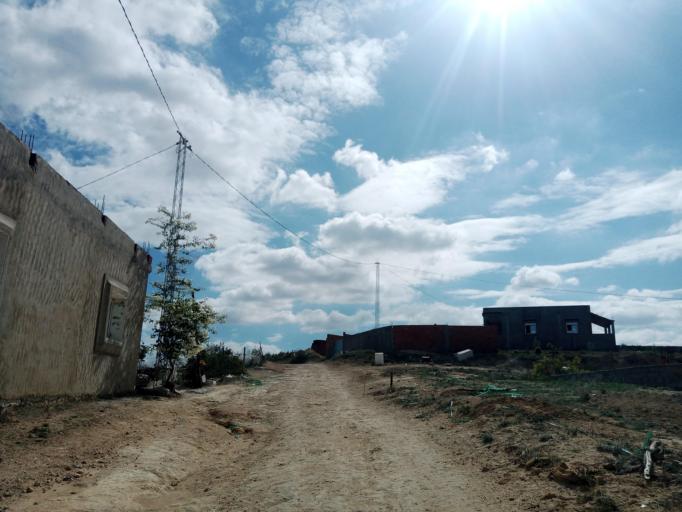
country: TN
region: Tunis
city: Oued Lill
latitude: 36.8098
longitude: 9.9827
